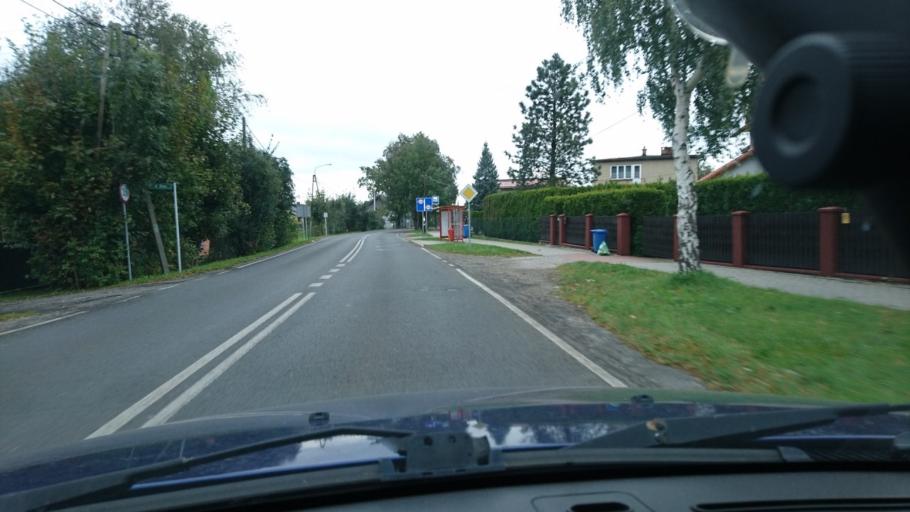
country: PL
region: Silesian Voivodeship
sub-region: Powiat bielski
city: Jaworze
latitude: 49.8014
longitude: 18.9837
